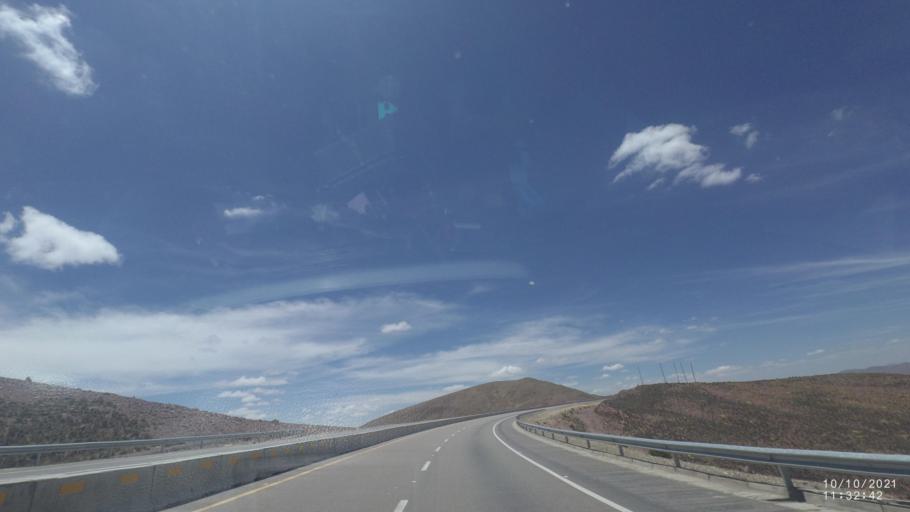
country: BO
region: Cochabamba
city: Colchani
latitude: -17.6383
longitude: -66.8556
